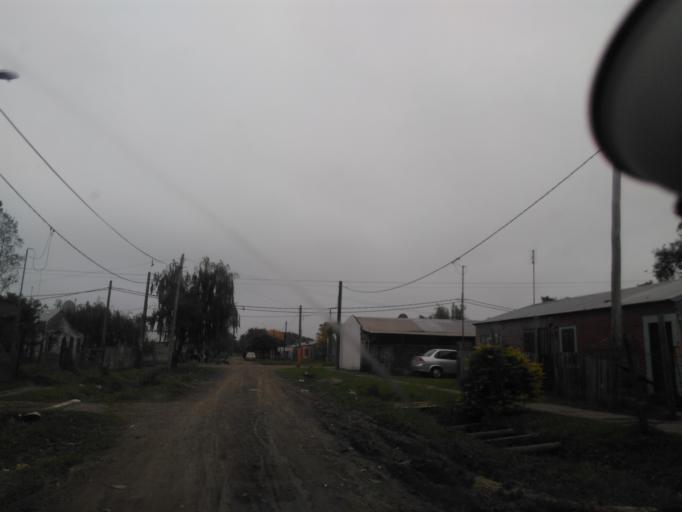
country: AR
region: Chaco
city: Fontana
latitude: -27.4010
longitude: -58.9918
